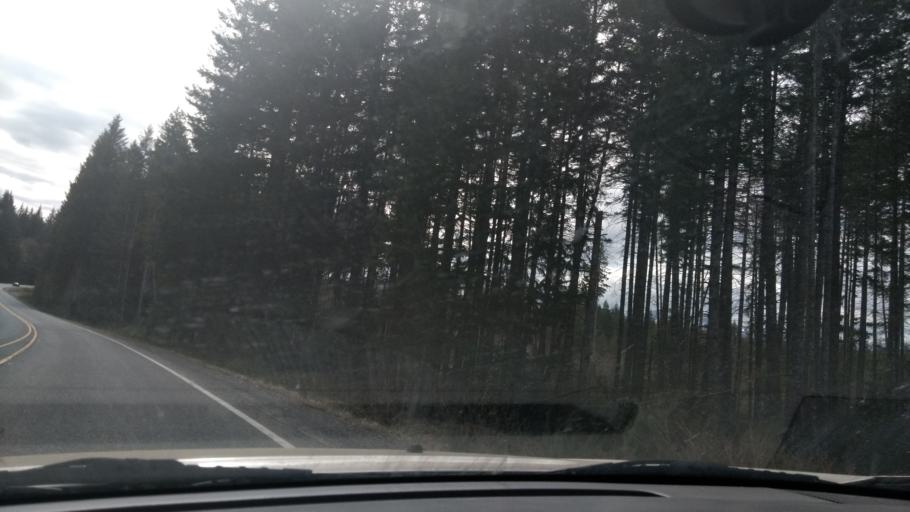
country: CA
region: British Columbia
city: Campbell River
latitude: 49.9758
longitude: -125.4418
